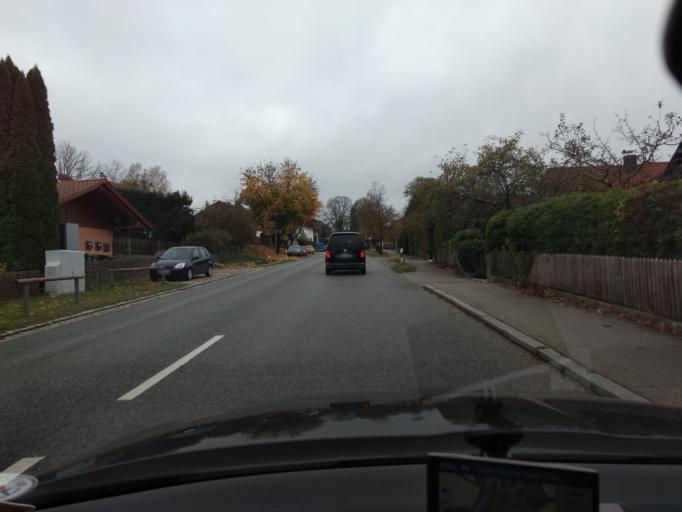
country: DE
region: Bavaria
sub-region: Upper Bavaria
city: Konigsdorf
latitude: 47.8204
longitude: 11.4833
